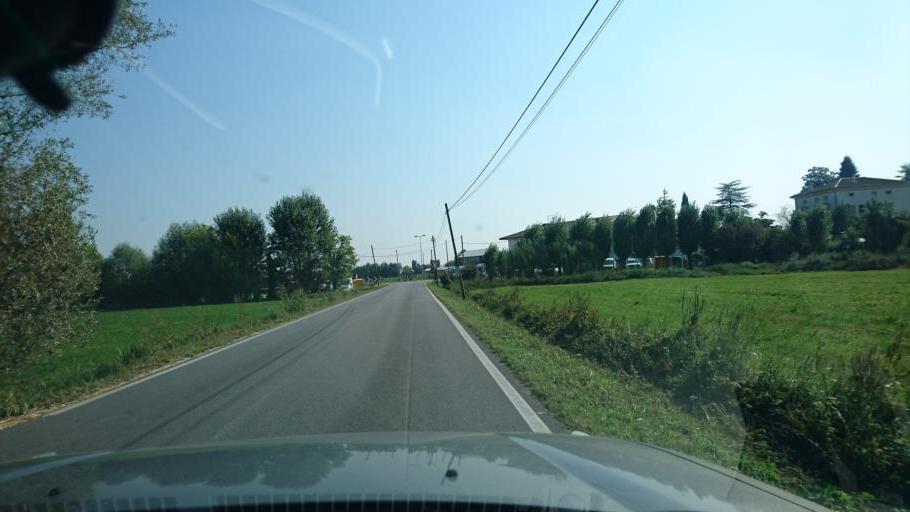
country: IT
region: Veneto
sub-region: Provincia di Vicenza
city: Camisano Vicentino
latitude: 45.5428
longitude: 11.7189
